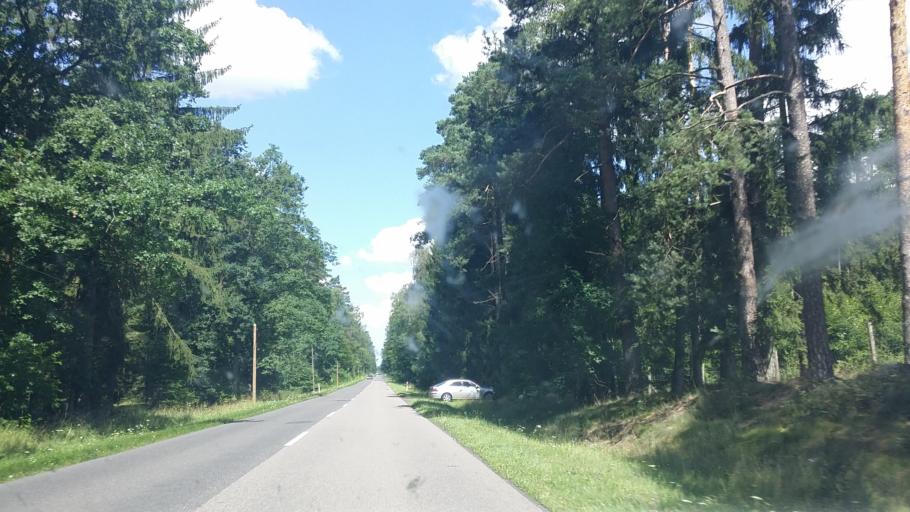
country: PL
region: West Pomeranian Voivodeship
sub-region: Powiat swidwinski
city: Slawoborze
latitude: 53.9364
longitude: 15.6774
